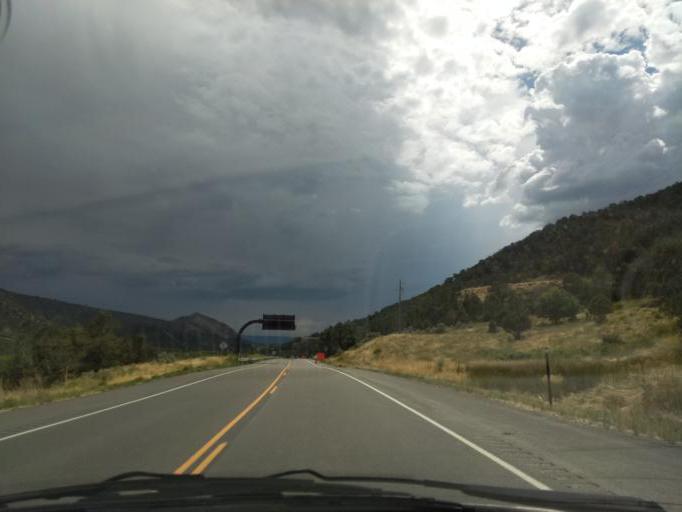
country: US
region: Colorado
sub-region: Delta County
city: Paonia
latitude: 38.9110
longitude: -107.5573
